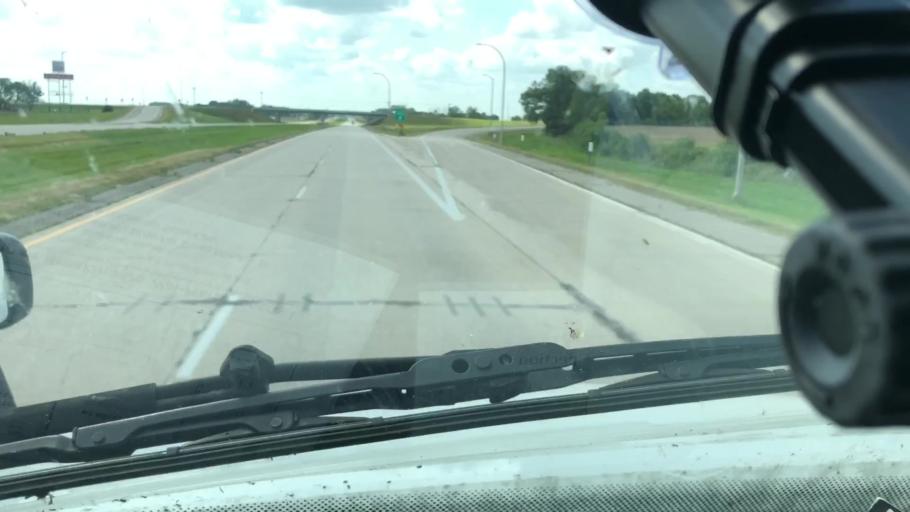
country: US
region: Minnesota
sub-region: Mower County
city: Grand Meadow
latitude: 43.7134
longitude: -92.6966
